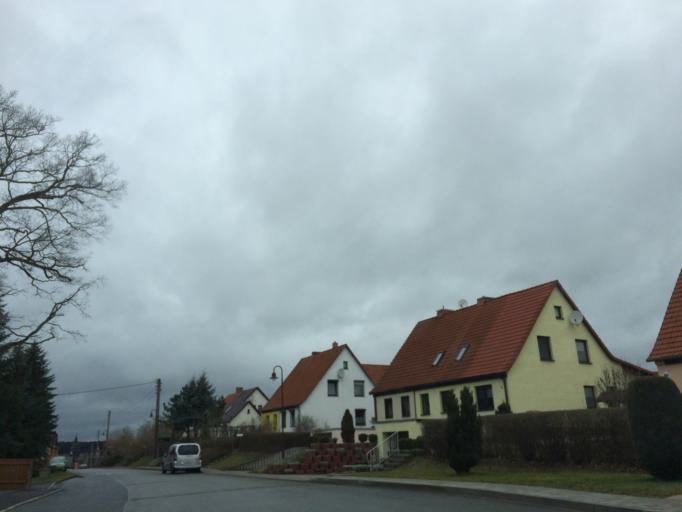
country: DE
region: Thuringia
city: Knau
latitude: 50.6497
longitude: 11.7253
